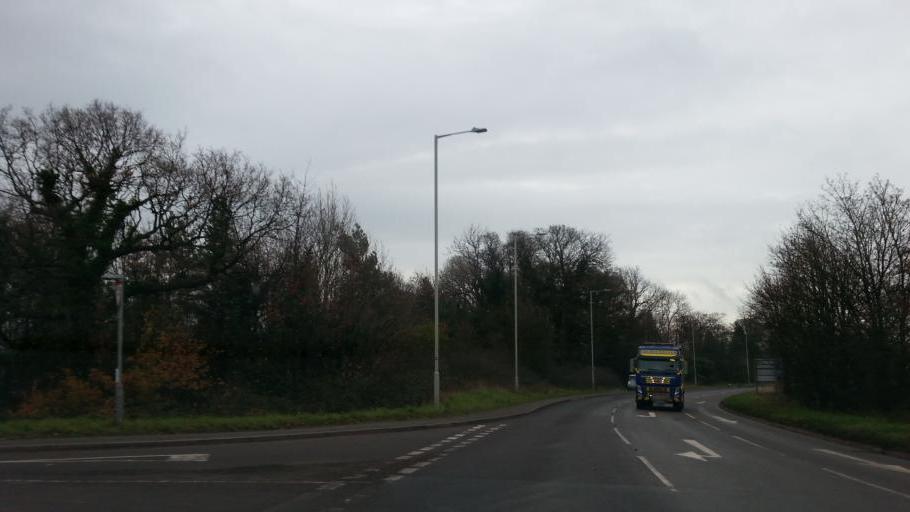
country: GB
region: England
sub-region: Telford and Wrekin
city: Wellington
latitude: 52.6922
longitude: -2.5417
